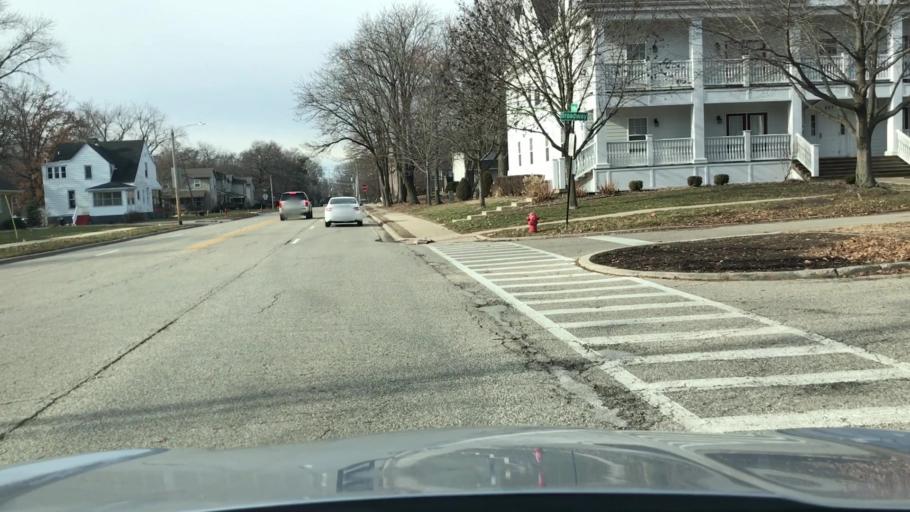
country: US
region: Illinois
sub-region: McLean County
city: Normal
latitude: 40.5050
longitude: -88.9855
